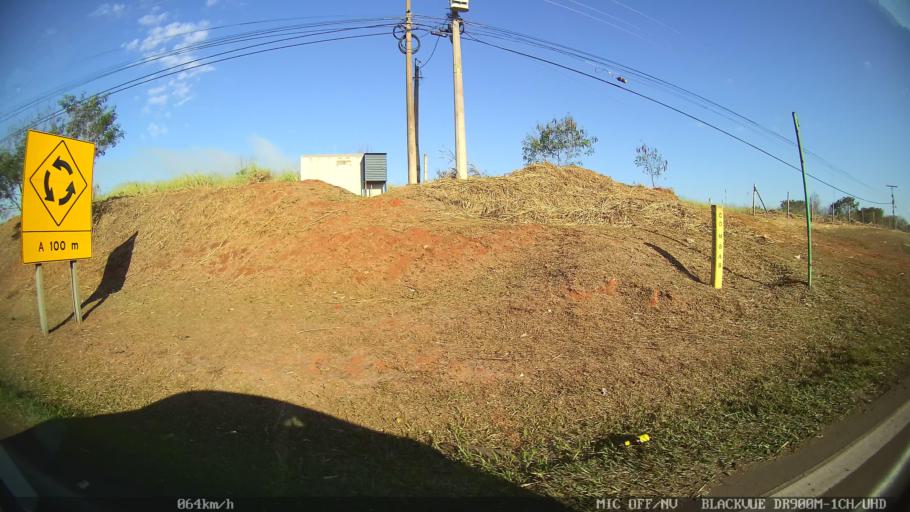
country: BR
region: Sao Paulo
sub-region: Piracicaba
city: Piracicaba
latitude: -22.6649
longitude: -47.6188
